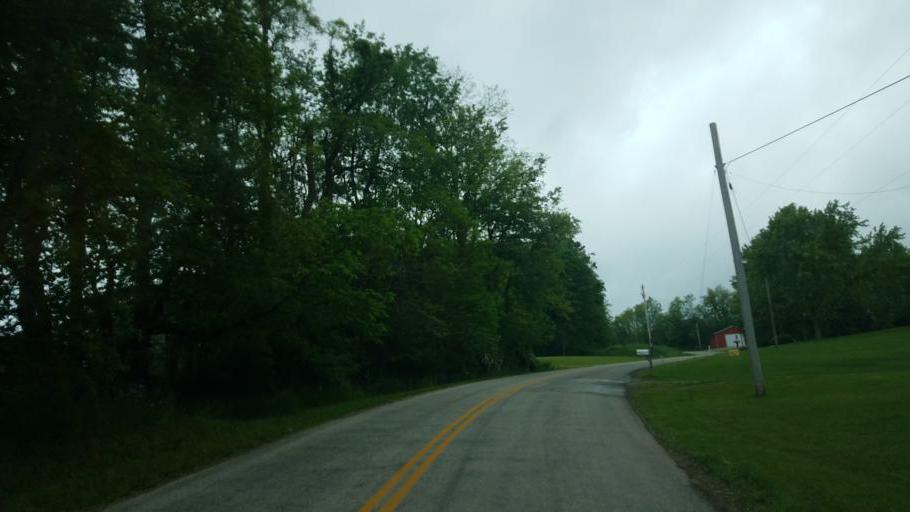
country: US
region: Ohio
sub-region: Ashland County
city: Ashland
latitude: 40.7637
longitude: -82.3490
